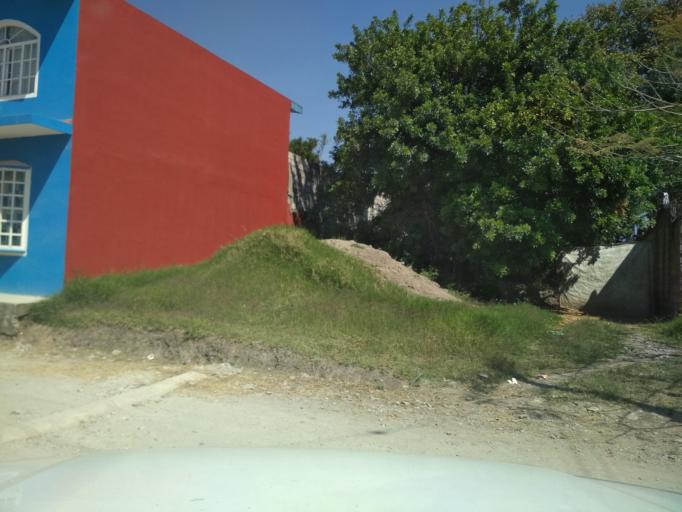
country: MX
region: Veracruz
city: Jalapilla
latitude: 18.8187
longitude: -97.0853
